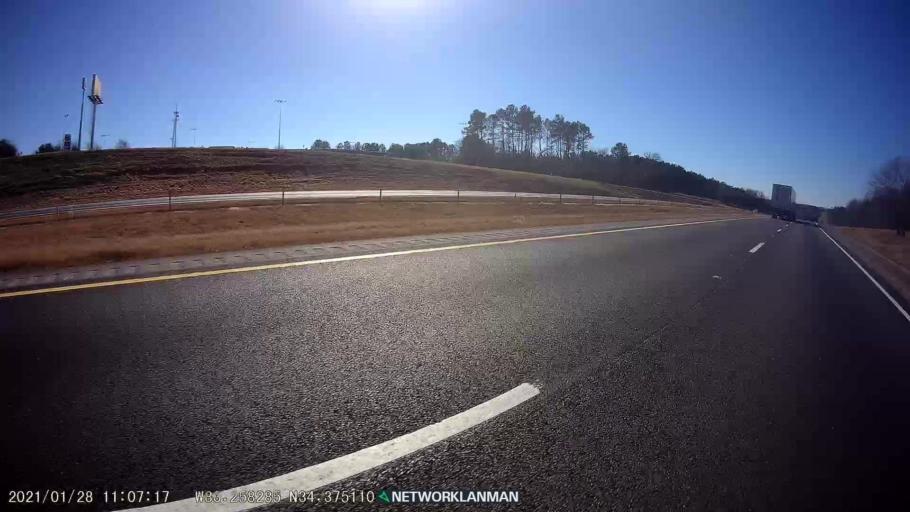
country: US
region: Georgia
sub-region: Franklin County
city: Carnesville
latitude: 34.3740
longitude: -83.2582
